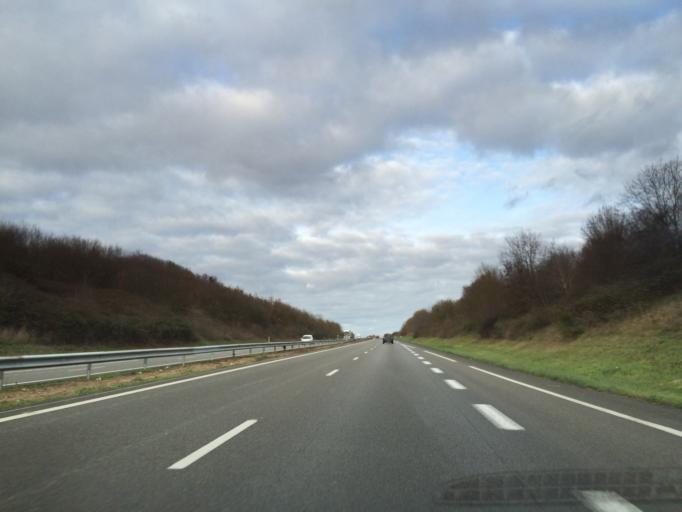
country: FR
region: Poitou-Charentes
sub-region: Departement de la Charente-Maritime
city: Saint-Jean-d'Angely
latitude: 45.9716
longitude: -0.5480
